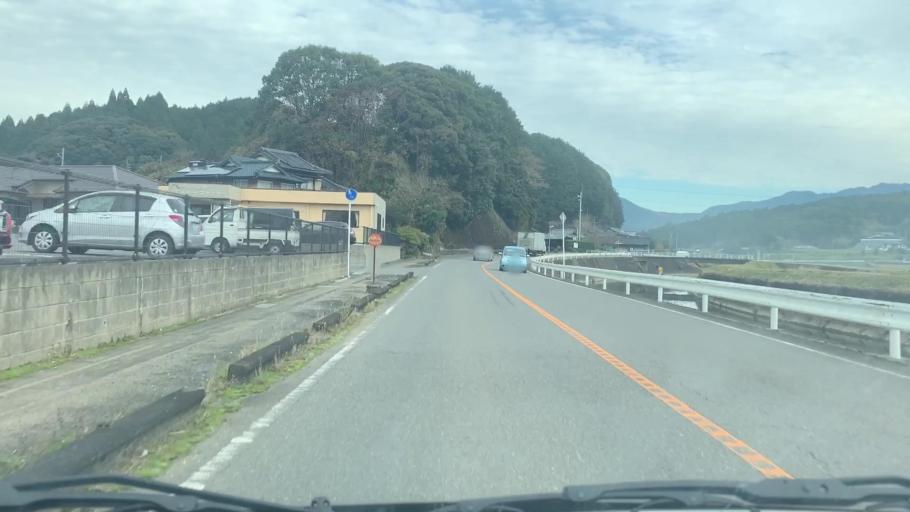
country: JP
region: Saga Prefecture
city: Takeocho-takeo
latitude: 33.2298
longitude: 129.9643
